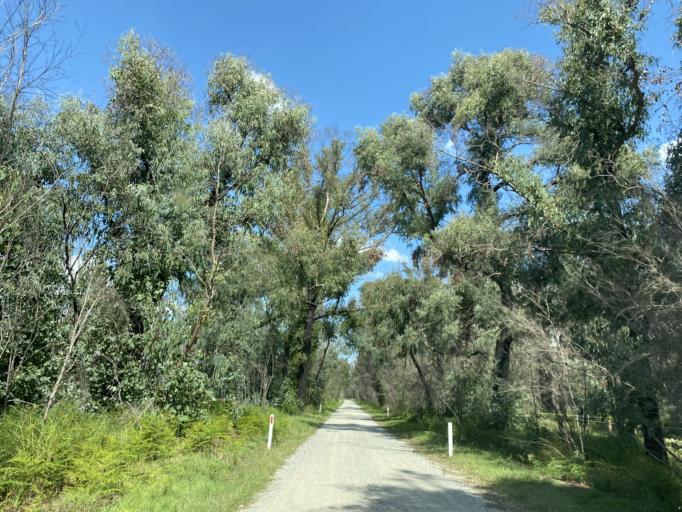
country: AU
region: Victoria
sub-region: Cardinia
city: Bunyip
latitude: -38.0059
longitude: 145.7408
